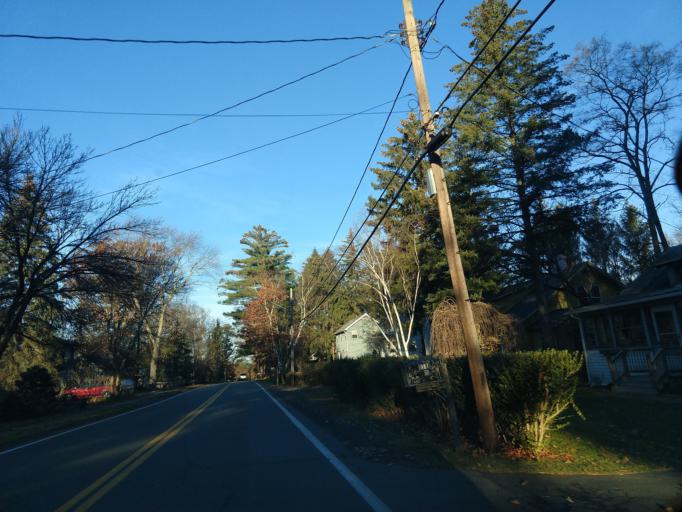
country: US
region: New York
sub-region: Tompkins County
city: Cayuga Heights
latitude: 42.4706
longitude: -76.4816
